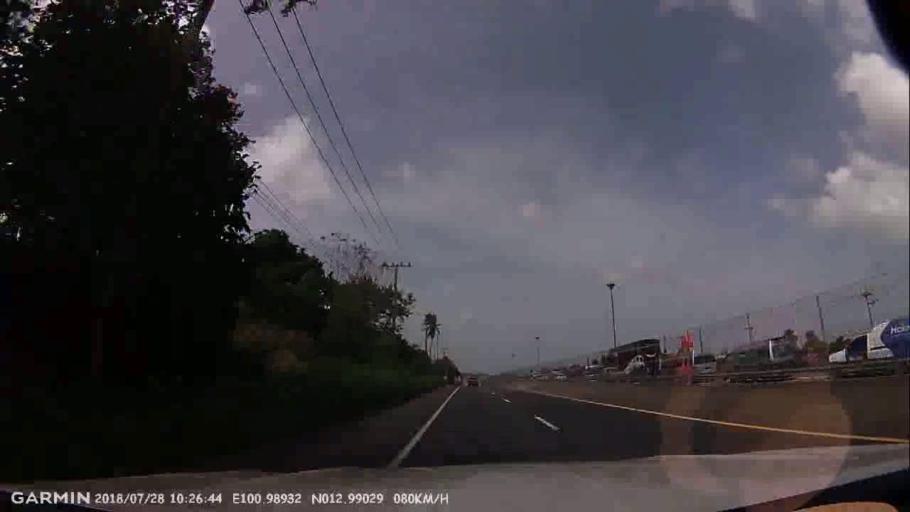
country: TH
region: Chon Buri
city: Ban Talat Bueng
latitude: 12.9906
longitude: 100.9895
